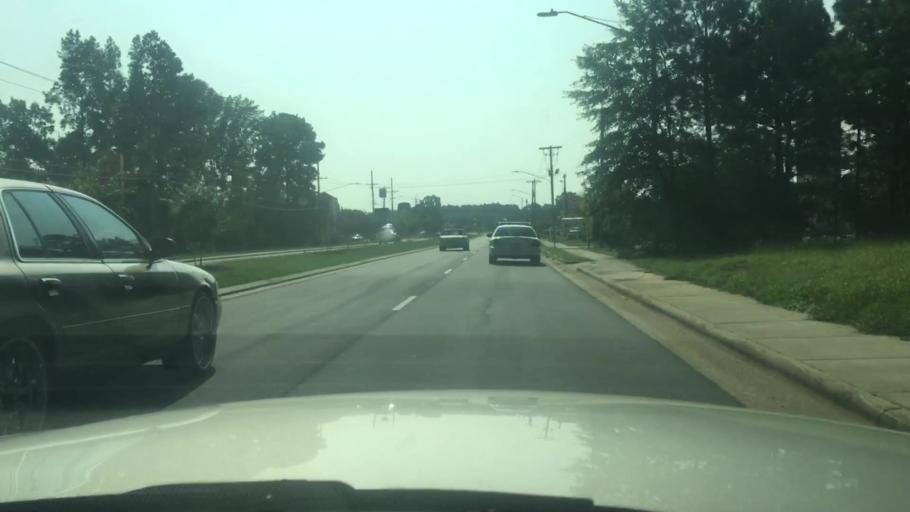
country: US
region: North Carolina
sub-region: Cumberland County
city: Vander
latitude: 35.0098
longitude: -78.8292
